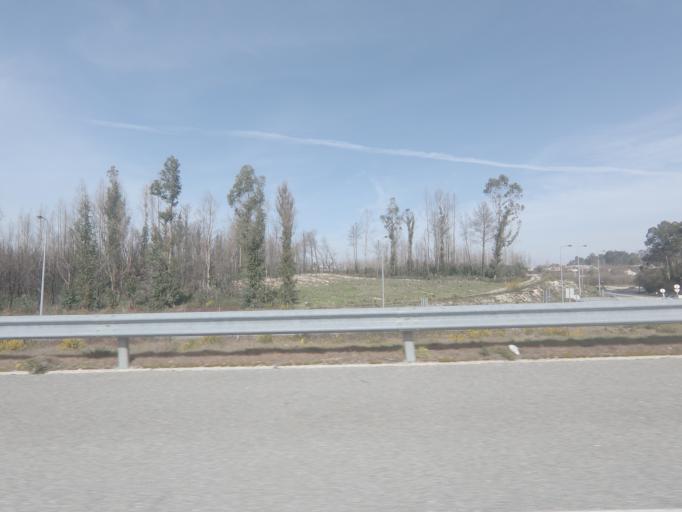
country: PT
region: Viseu
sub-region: Oliveira de Frades
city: Oliveira de Frades
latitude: 40.6834
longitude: -8.2005
